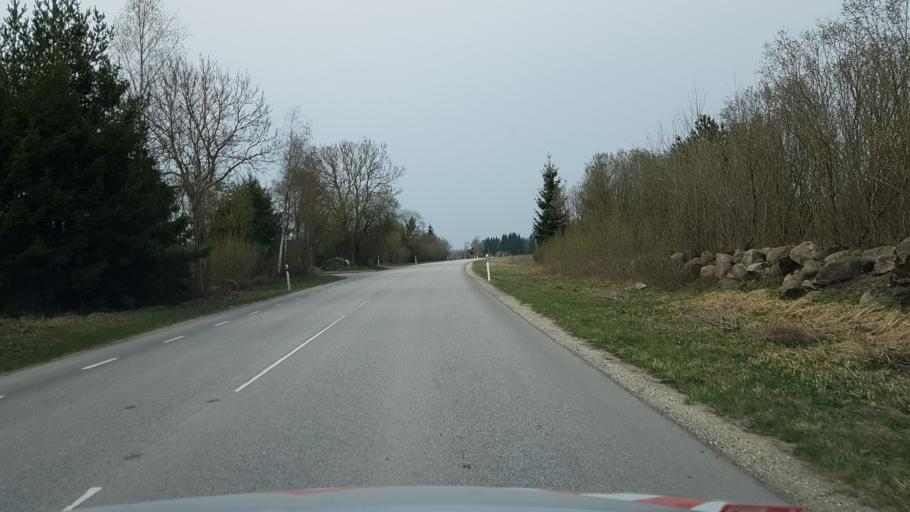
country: EE
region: Harju
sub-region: Raasiku vald
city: Arukula
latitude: 59.3793
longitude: 25.0087
